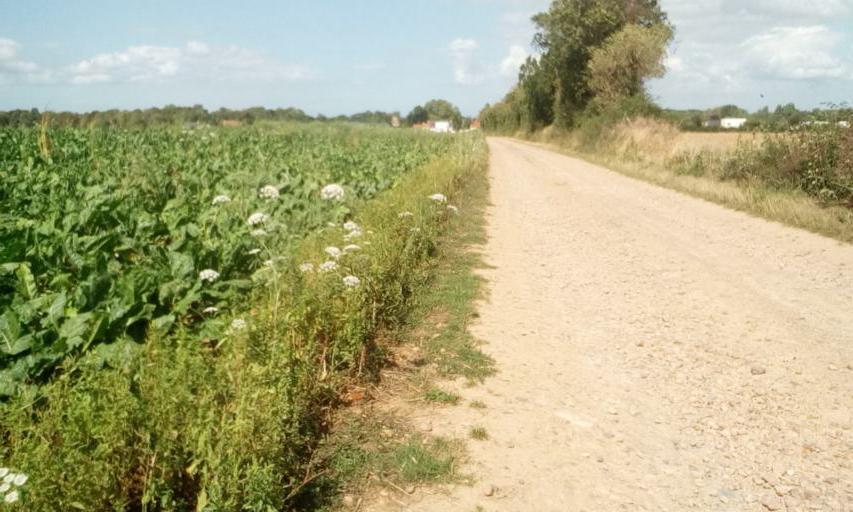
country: FR
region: Lower Normandy
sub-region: Departement du Calvados
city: Bellengreville
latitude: 49.1055
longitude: -0.2262
